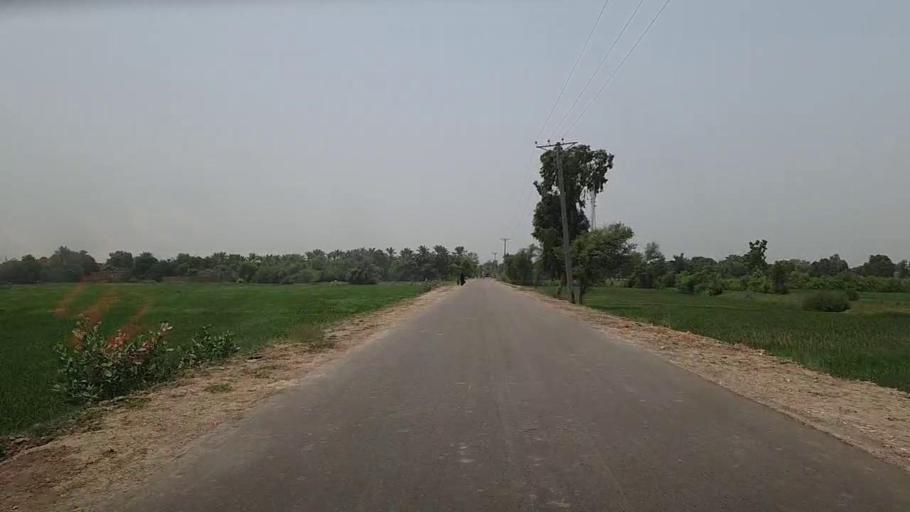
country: PK
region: Sindh
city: Sita Road
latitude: 27.0432
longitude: 67.9003
